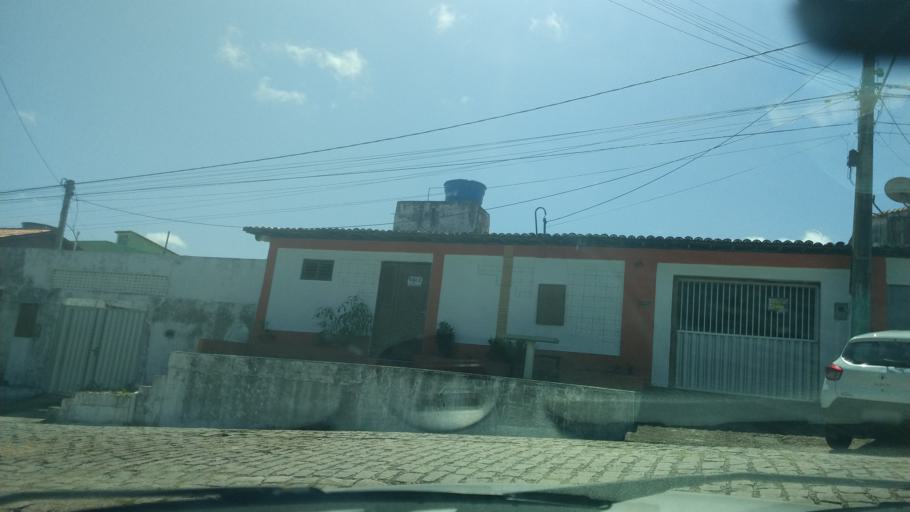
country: BR
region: Rio Grande do Norte
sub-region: Parnamirim
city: Parnamirim
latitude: -5.9477
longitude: -35.1565
